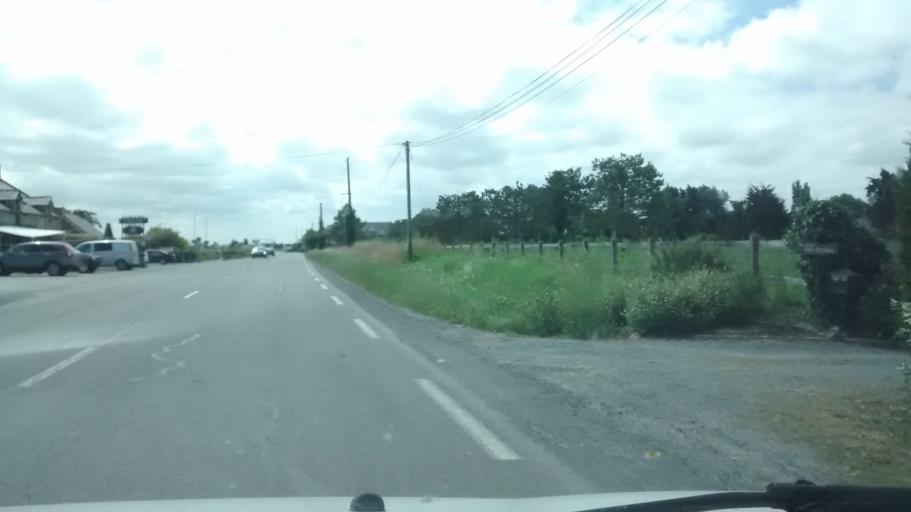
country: FR
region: Brittany
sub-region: Departement d'Ille-et-Vilaine
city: Saint-Meloir-des-Ondes
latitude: 48.6335
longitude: -1.8655
